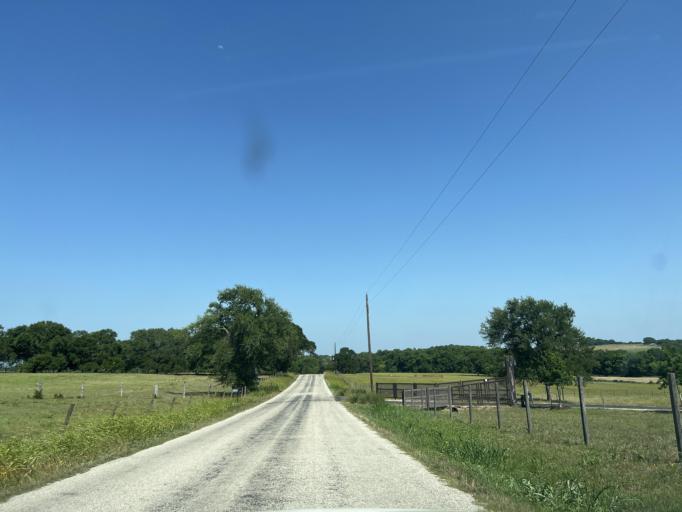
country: US
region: Texas
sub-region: Washington County
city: Brenham
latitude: 30.1747
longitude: -96.3465
